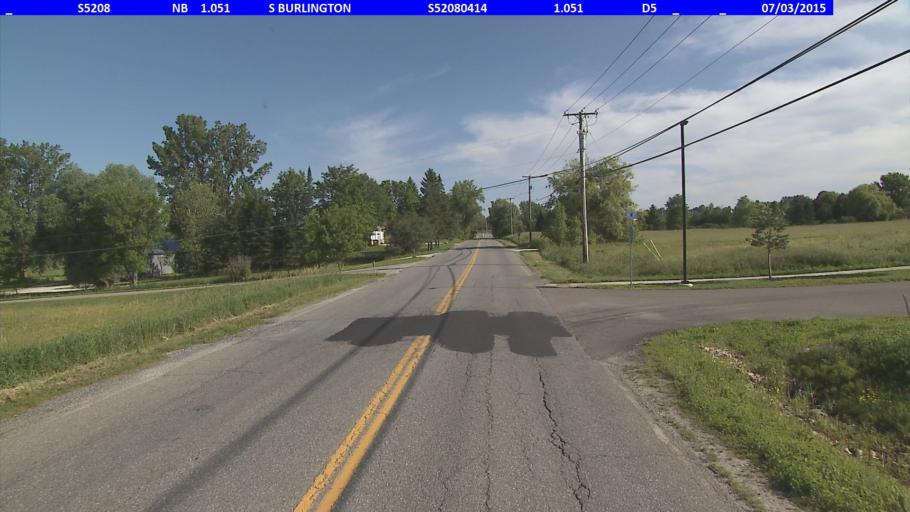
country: US
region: Vermont
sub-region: Chittenden County
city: South Burlington
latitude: 44.4259
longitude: -73.1742
